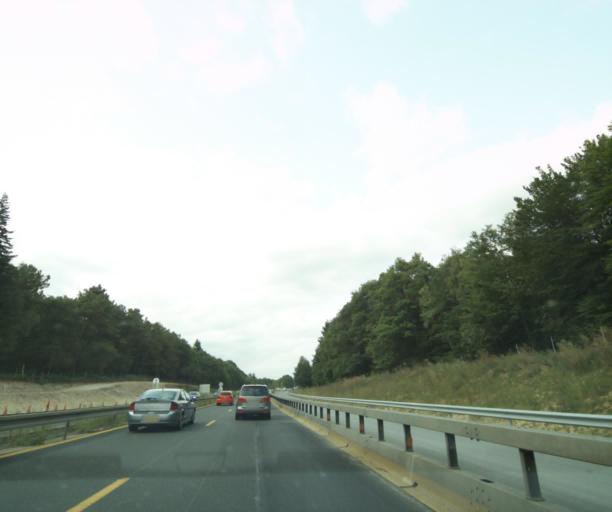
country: FR
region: Centre
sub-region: Departement d'Indre-et-Loire
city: Chambray-les-Tours
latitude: 47.3130
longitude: 0.6894
